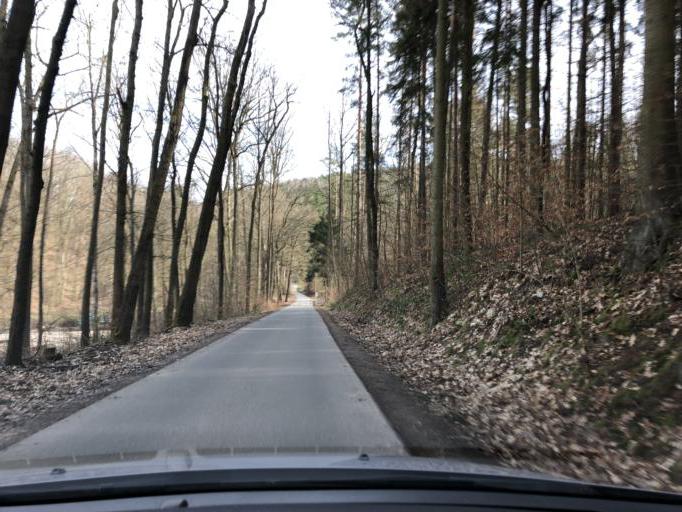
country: DE
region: Thuringia
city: Tautenhain
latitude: 50.9508
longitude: 11.9096
